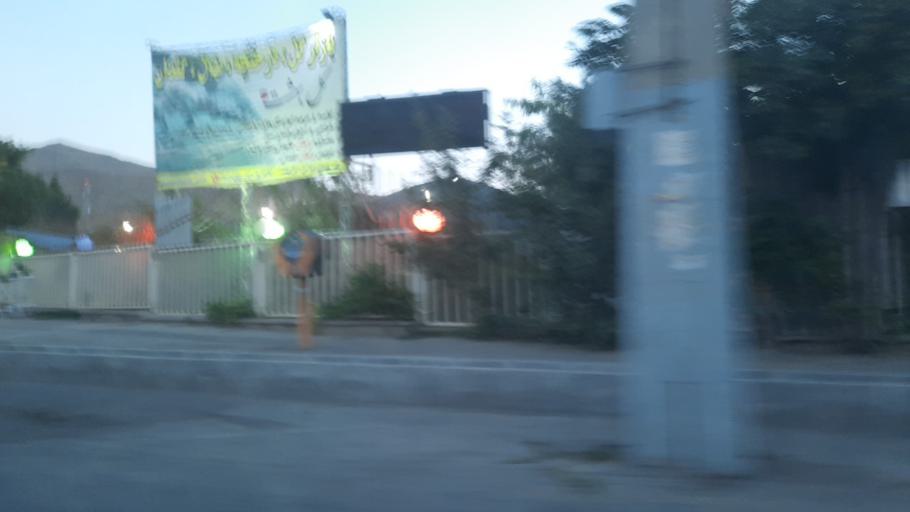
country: IR
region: Markazi
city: Arak
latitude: 34.0741
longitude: 49.7026
